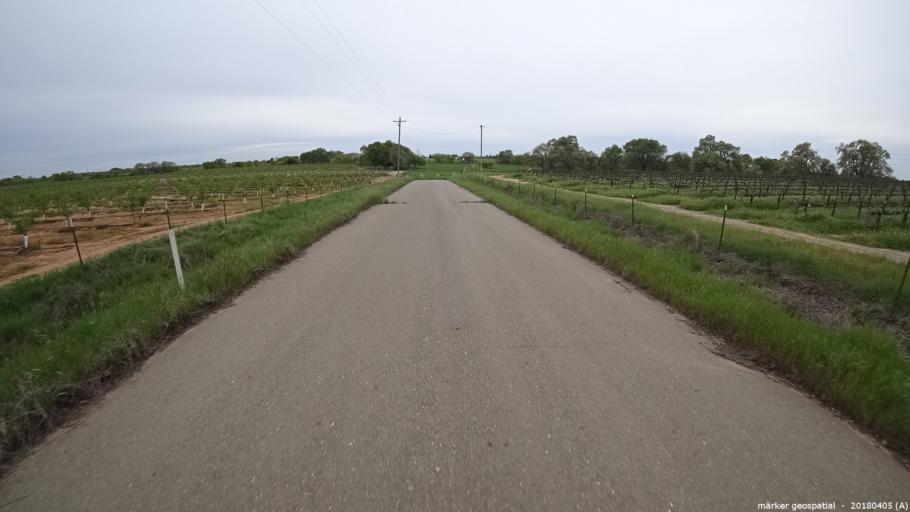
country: US
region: California
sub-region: Sacramento County
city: Herald
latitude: 38.3213
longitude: -121.2136
